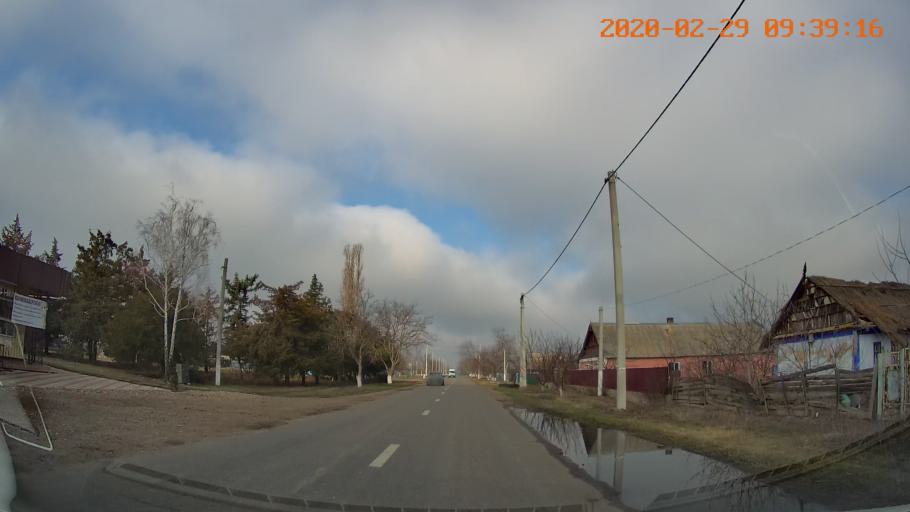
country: MD
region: Telenesti
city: Crasnoe
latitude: 46.6347
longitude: 29.8568
